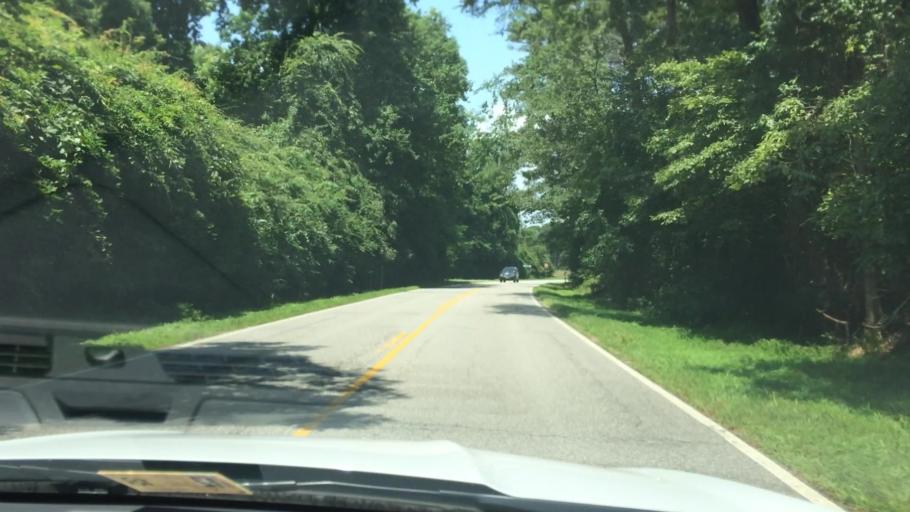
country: US
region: Virginia
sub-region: York County
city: Yorktown
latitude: 37.2204
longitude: -76.5061
